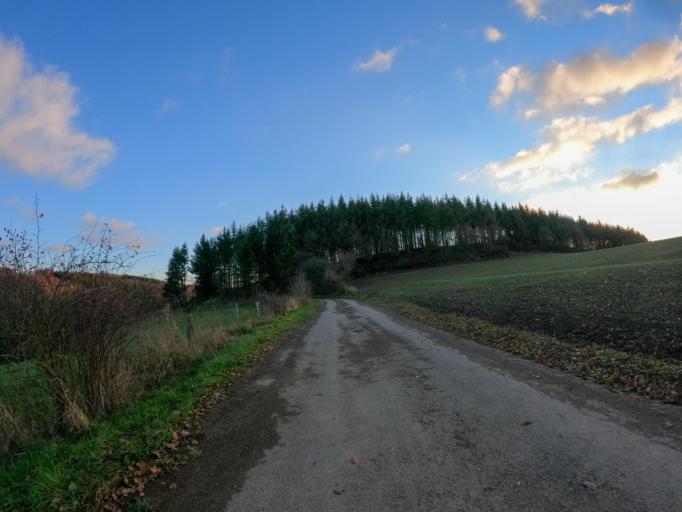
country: LU
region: Diekirch
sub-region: Canton de Wiltz
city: Bavigne
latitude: 49.9230
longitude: 5.8547
